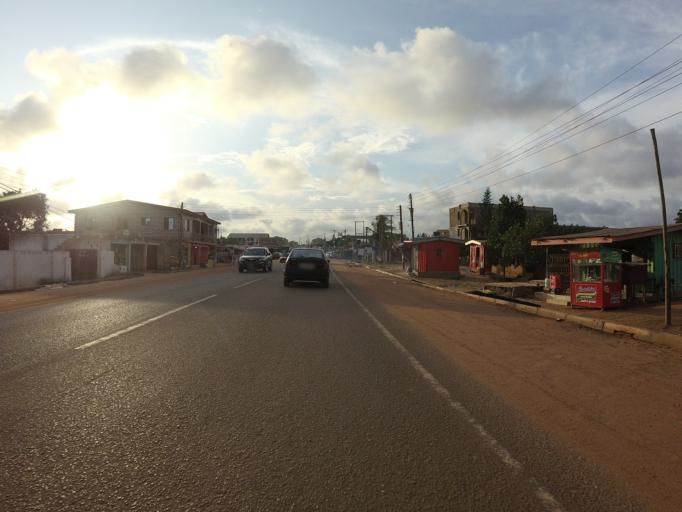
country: GH
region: Greater Accra
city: Teshi Old Town
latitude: 5.5956
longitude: -0.1231
